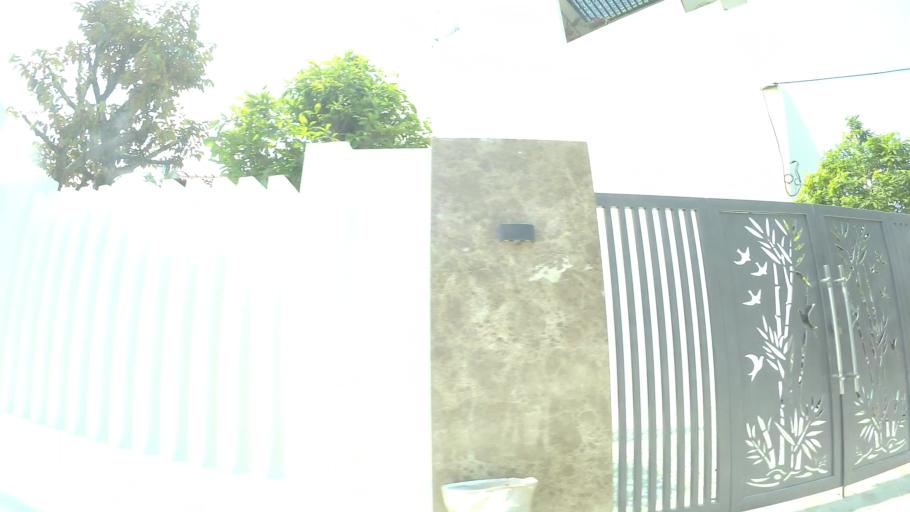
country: VN
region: Da Nang
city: Cam Le
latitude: 16.0138
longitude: 108.2030
